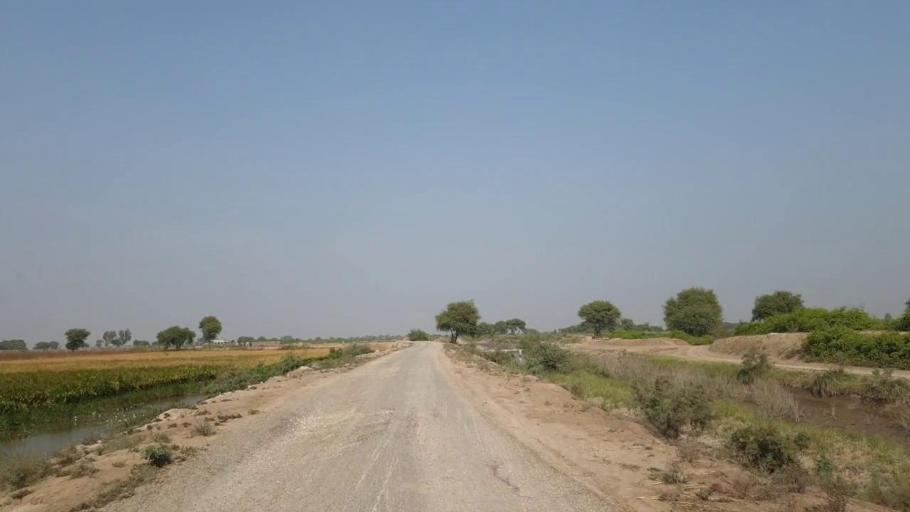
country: PK
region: Sindh
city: Matli
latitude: 24.9511
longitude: 68.5275
